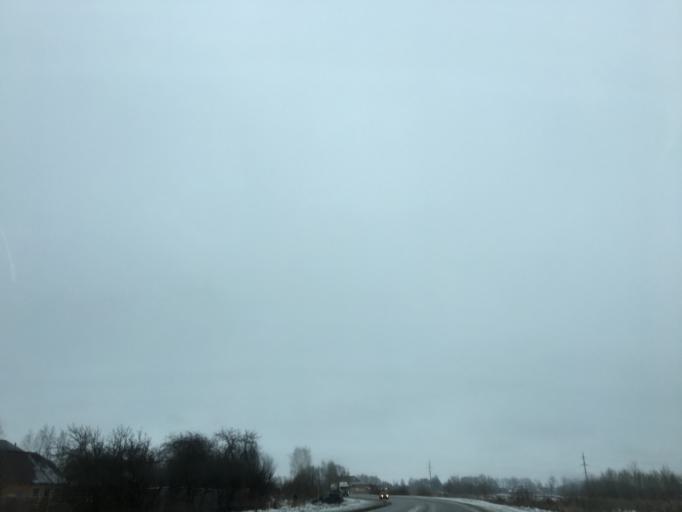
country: RU
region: Tula
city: Bolokhovo
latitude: 54.0554
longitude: 37.8079
